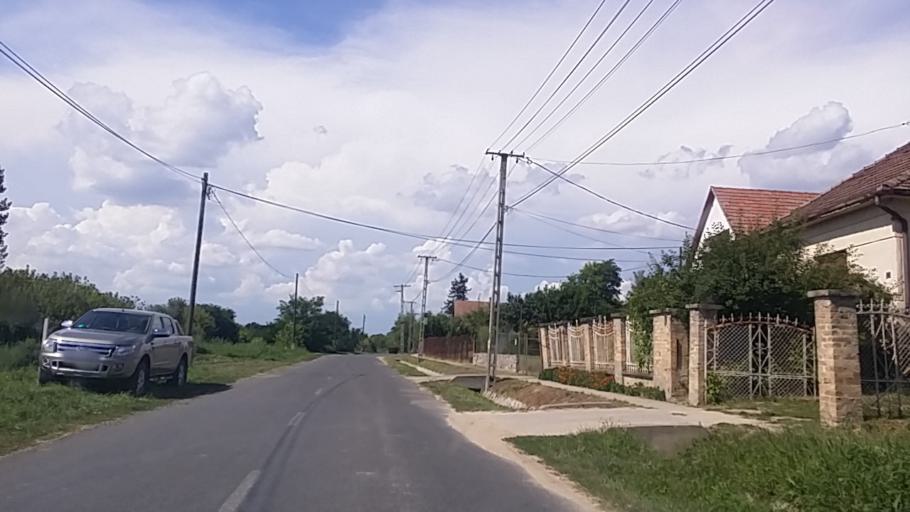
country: HU
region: Tolna
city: Hogyesz
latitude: 46.5285
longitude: 18.4455
